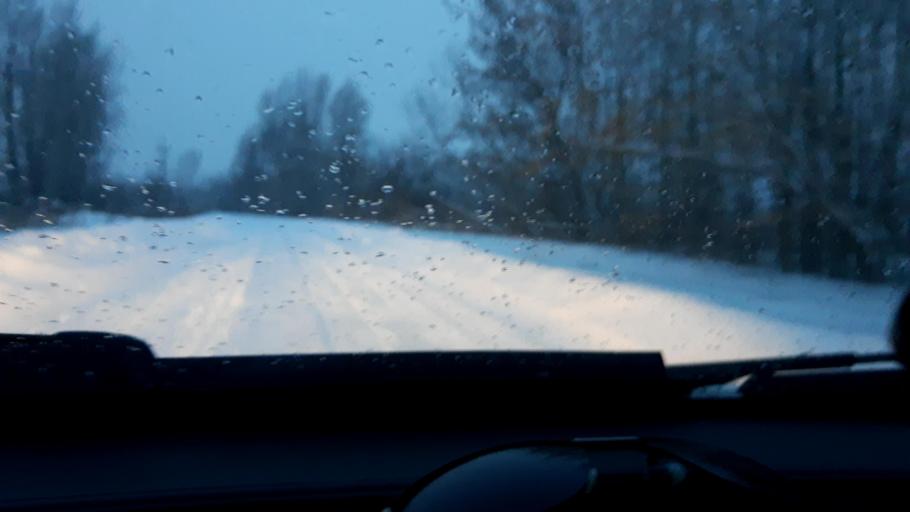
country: RU
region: Bashkortostan
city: Iglino
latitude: 54.7964
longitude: 56.2252
